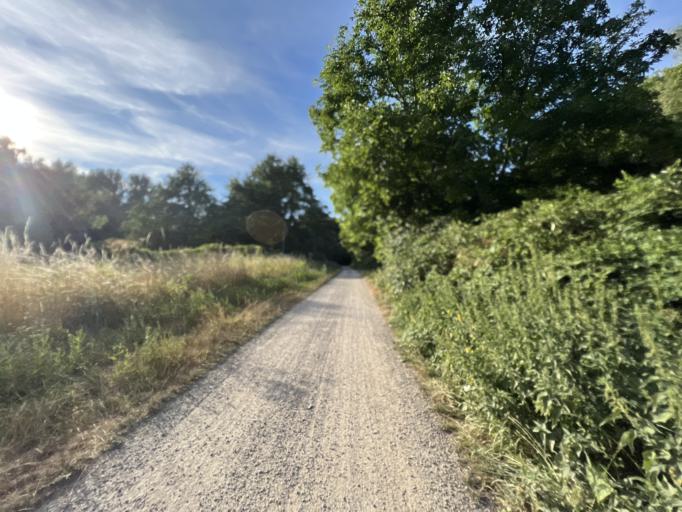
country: DE
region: North Rhine-Westphalia
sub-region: Regierungsbezirk Koln
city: Dueren
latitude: 50.8108
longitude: 6.4615
